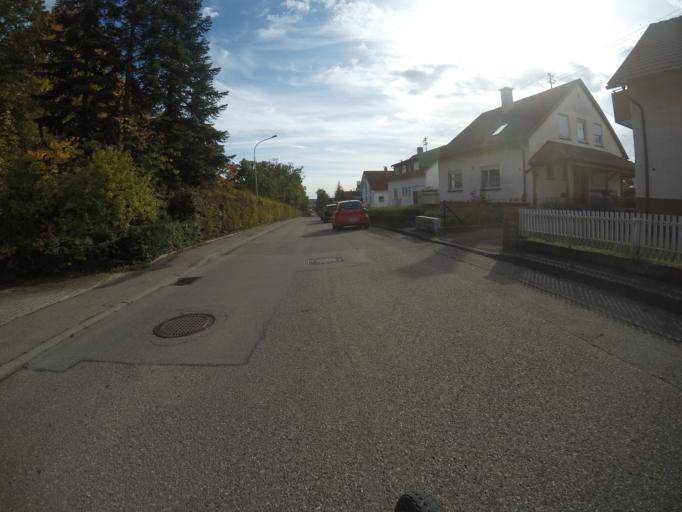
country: DE
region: Baden-Wuerttemberg
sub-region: Regierungsbezirk Stuttgart
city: Herrenberg
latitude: 48.5801
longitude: 8.8793
